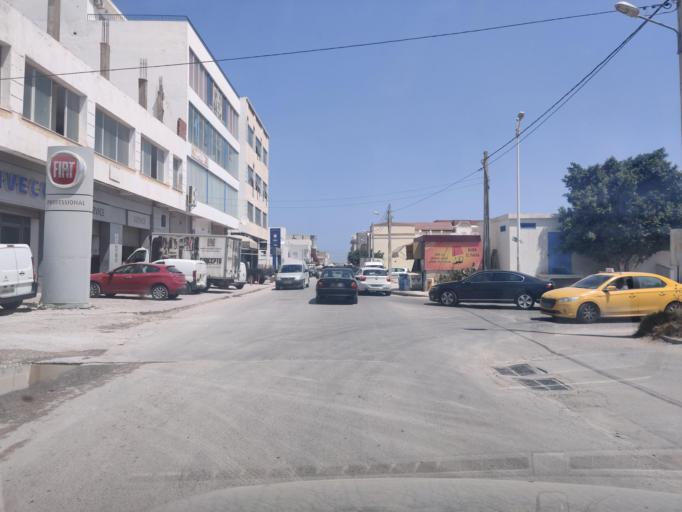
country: TN
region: Tunis
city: Al Marsa
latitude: 36.8703
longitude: 10.2959
